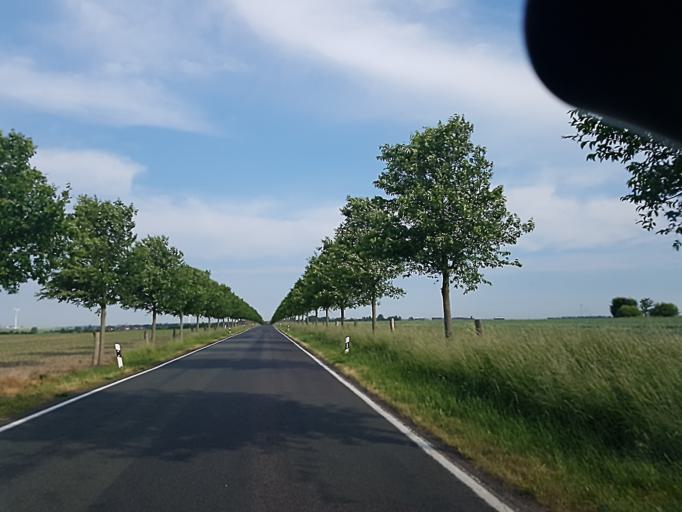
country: DE
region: Saxony-Anhalt
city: Kropstadt
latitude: 51.9906
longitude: 12.7930
